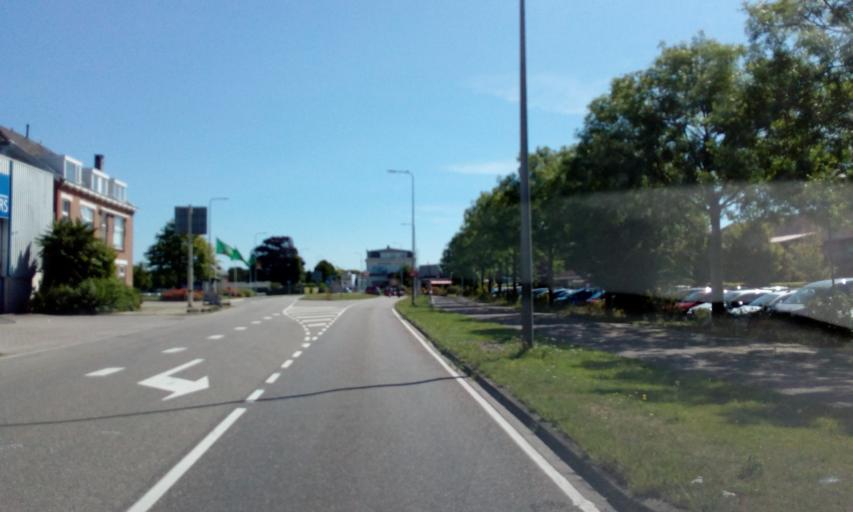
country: NL
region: South Holland
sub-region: Gemeente Alphen aan den Rijn
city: Alphen aan den Rijn
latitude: 52.1412
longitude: 4.6463
